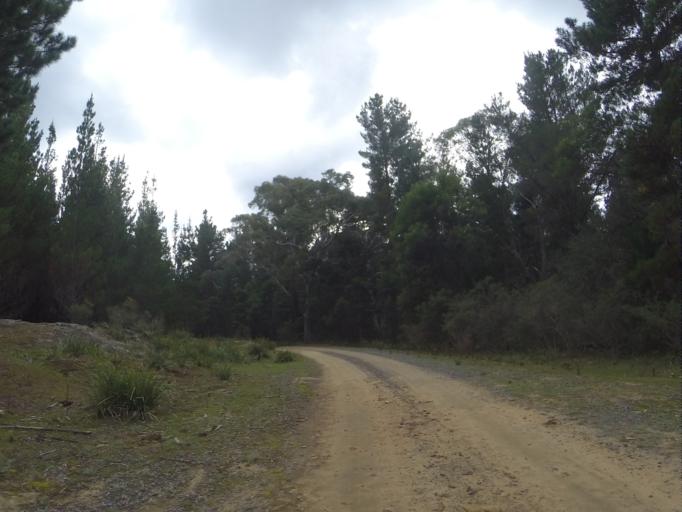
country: AU
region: New South Wales
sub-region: Wingecarribee
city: Moss Vale
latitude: -34.5241
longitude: 150.2547
